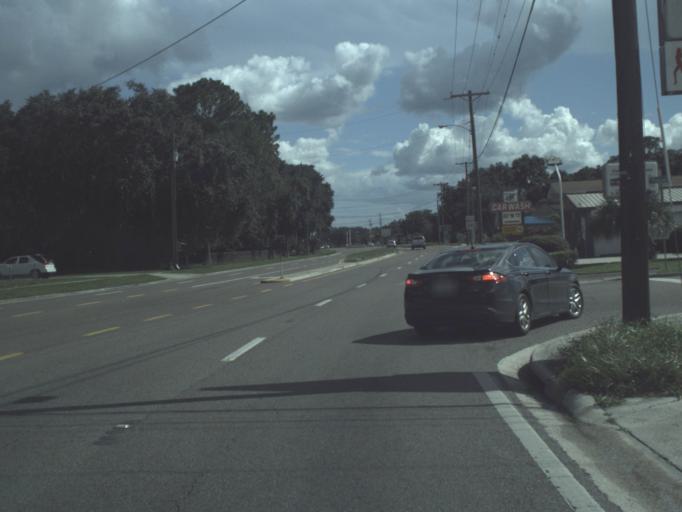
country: US
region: Florida
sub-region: Hillsborough County
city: Plant City
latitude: 28.0015
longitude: -82.1212
